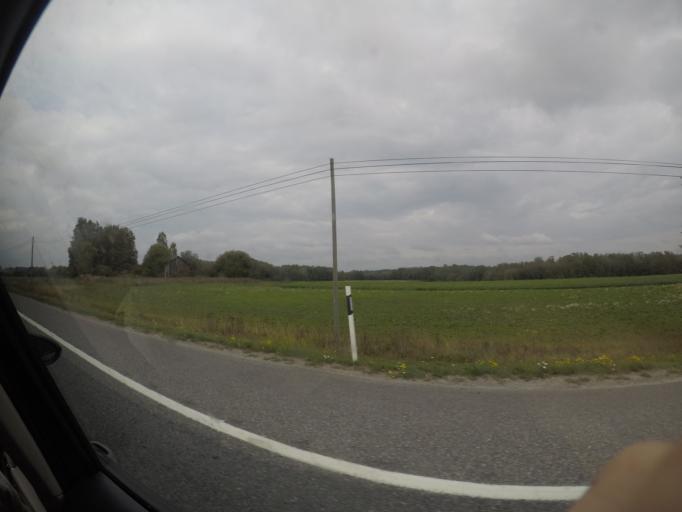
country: FI
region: Haeme
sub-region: Haemeenlinna
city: Haemeenlinna
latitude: 61.0317
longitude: 24.4164
